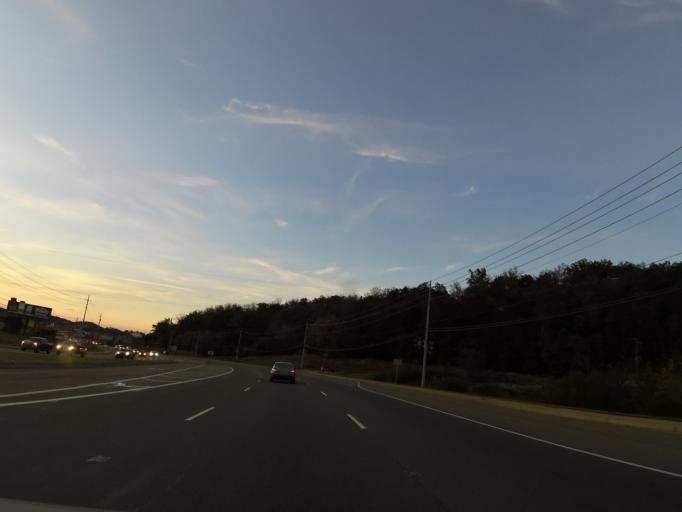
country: US
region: Tennessee
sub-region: Sevier County
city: Sevierville
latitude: 35.8860
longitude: -83.5733
